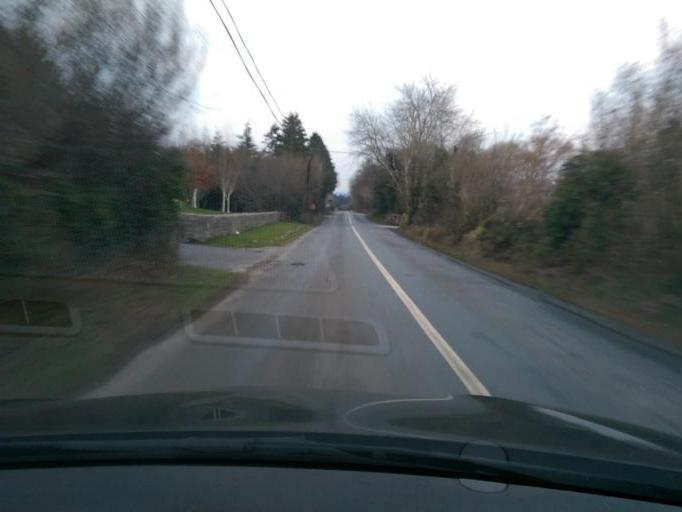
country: IE
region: Connaught
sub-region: County Galway
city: Moycullen
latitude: 53.3050
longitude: -9.1545
